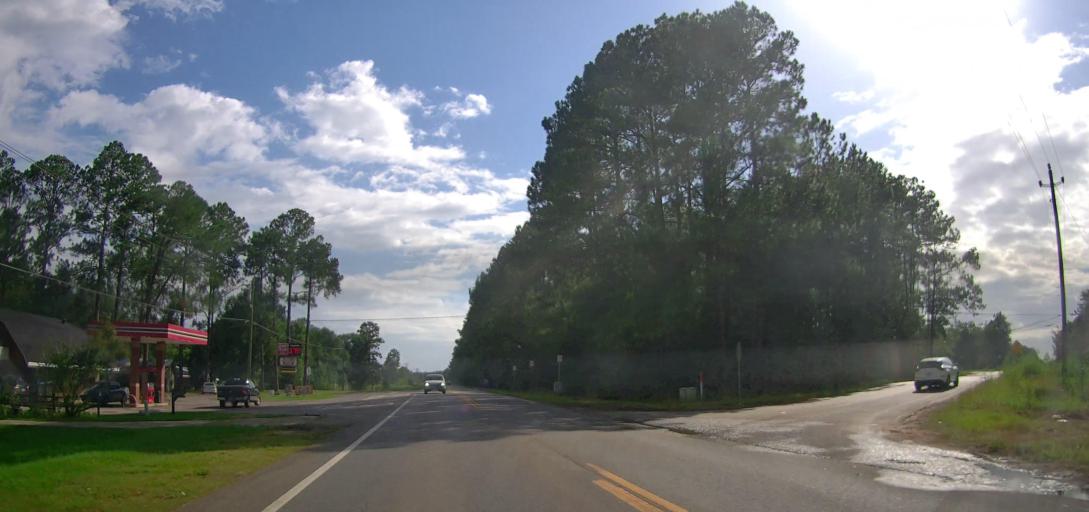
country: US
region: Georgia
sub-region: Coffee County
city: Douglas
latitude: 31.4668
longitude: -82.8812
